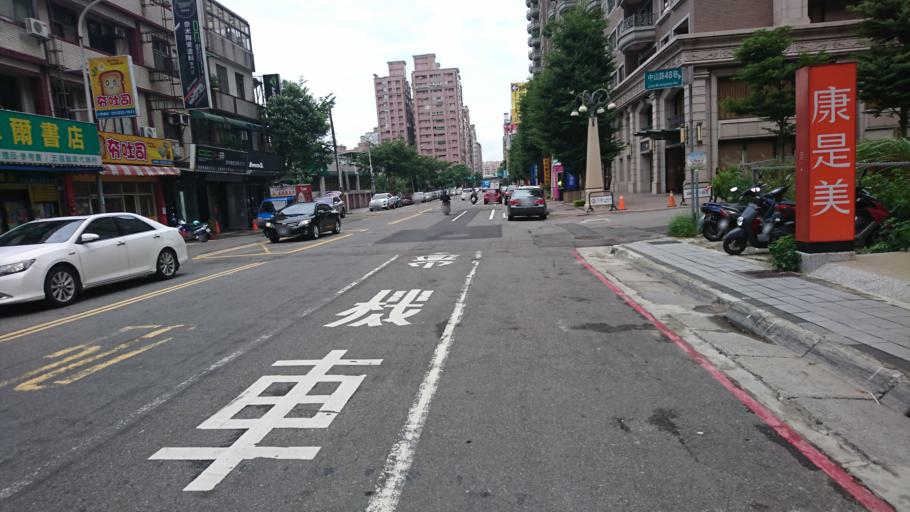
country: TW
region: Taiwan
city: Taoyuan City
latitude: 25.0533
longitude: 121.3000
